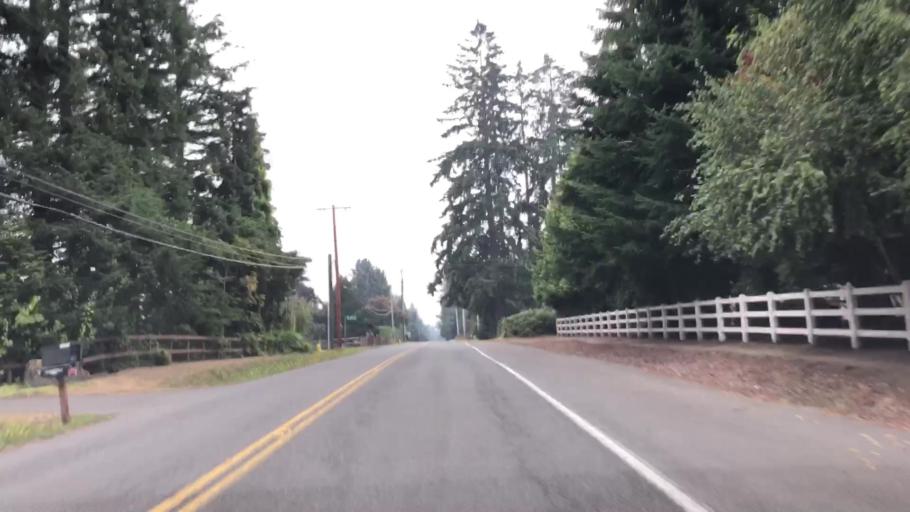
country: US
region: Washington
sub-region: King County
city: Cottage Lake
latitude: 47.7370
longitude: -122.1153
